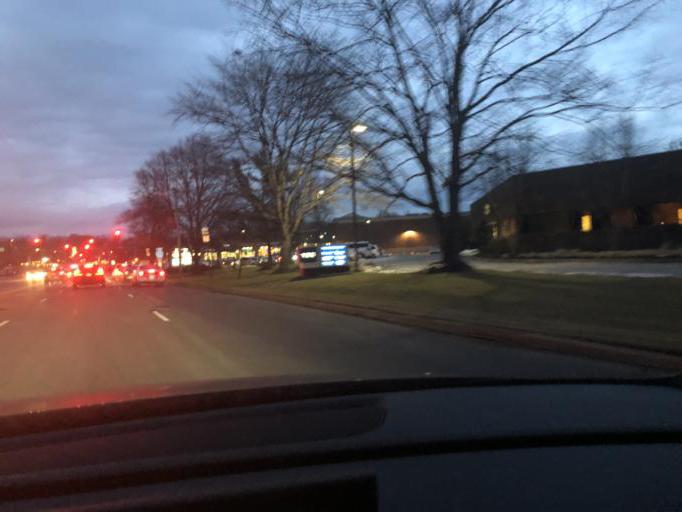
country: US
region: New Jersey
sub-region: Morris County
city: Florham Park
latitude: 40.7886
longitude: -74.3941
